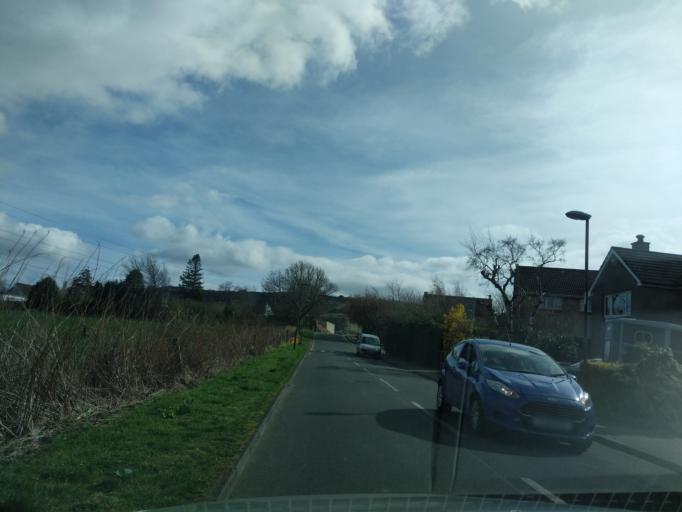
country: GB
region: Scotland
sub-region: Edinburgh
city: Currie
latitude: 55.9018
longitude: -3.2950
